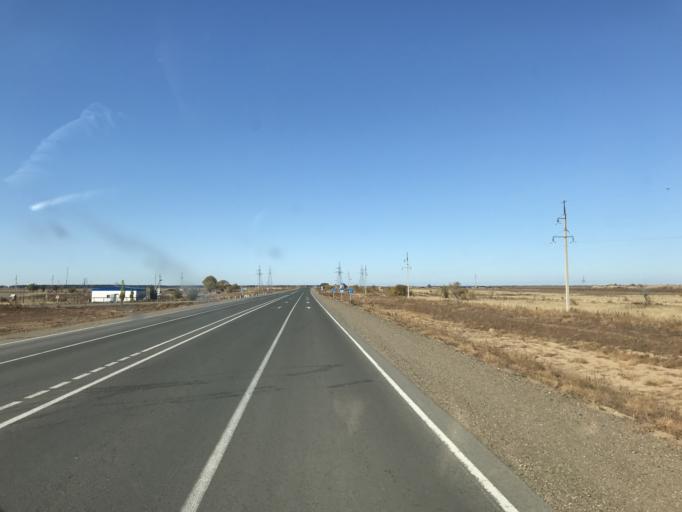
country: KZ
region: Pavlodar
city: Kurchatov
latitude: 51.0548
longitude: 79.1168
